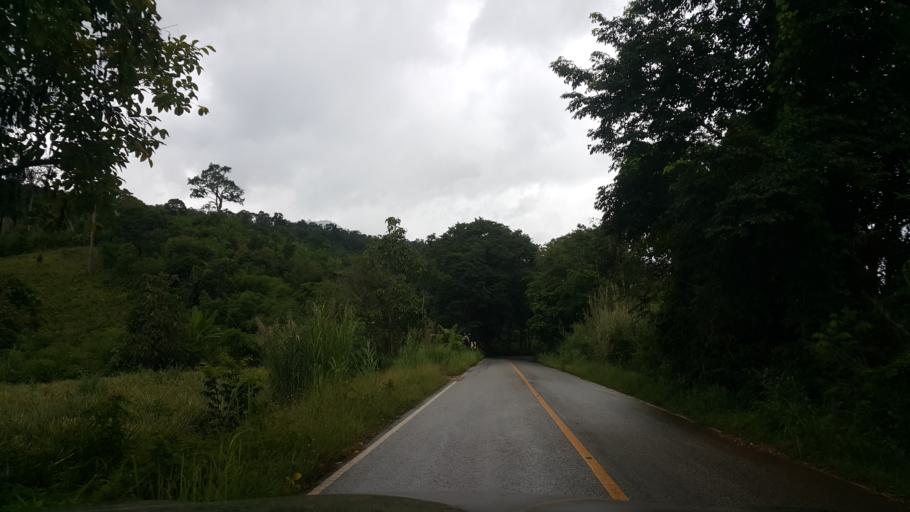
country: TH
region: Loei
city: Na Haeo
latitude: 17.4854
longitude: 100.8055
